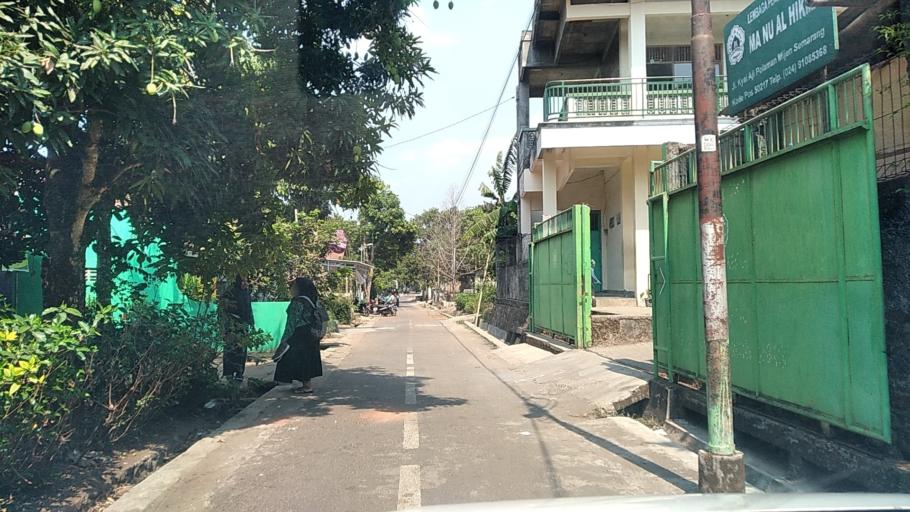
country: ID
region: Central Java
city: Ungaran
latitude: -7.0926
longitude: 110.3327
